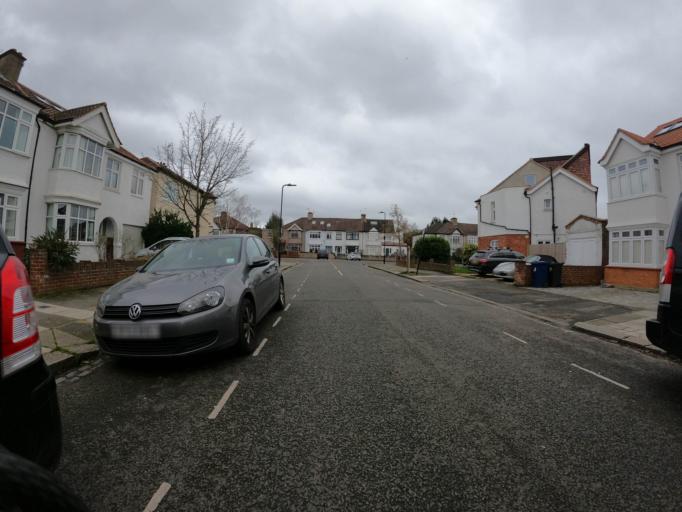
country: GB
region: England
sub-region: Greater London
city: Ealing
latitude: 51.5053
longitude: -0.3279
